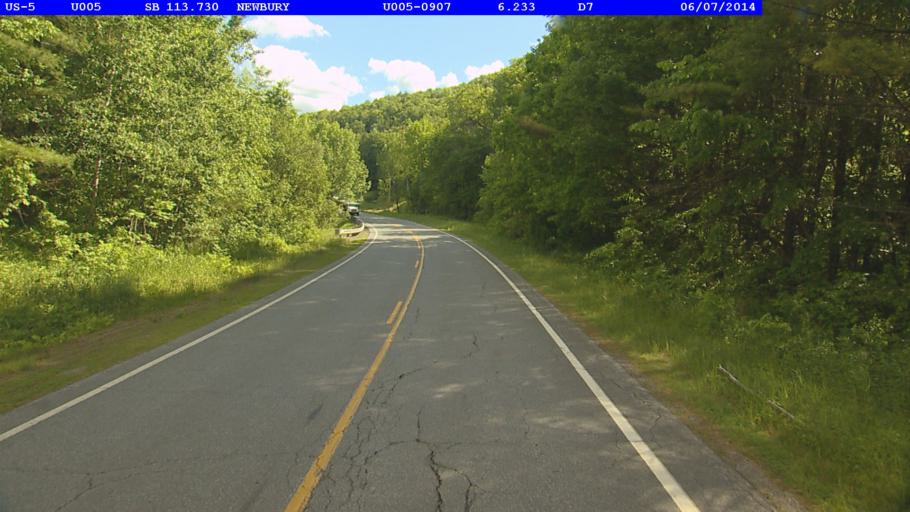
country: US
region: New Hampshire
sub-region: Grafton County
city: North Haverhill
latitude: 44.1101
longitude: -72.0568
